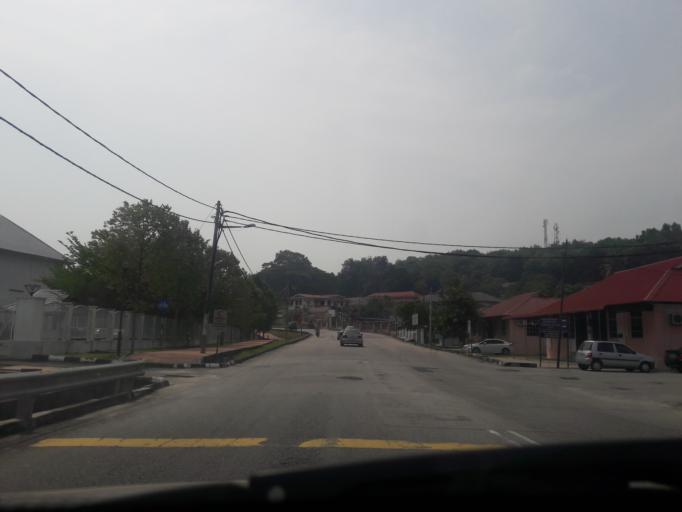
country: MY
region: Kedah
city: Kulim
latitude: 5.3685
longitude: 100.5576
